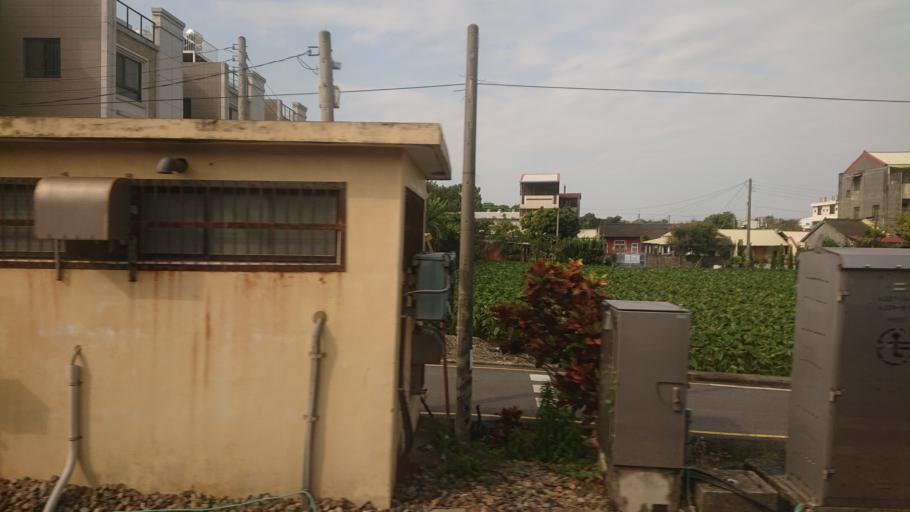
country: TW
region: Taiwan
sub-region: Nantou
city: Nantou
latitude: 23.8978
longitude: 120.5800
